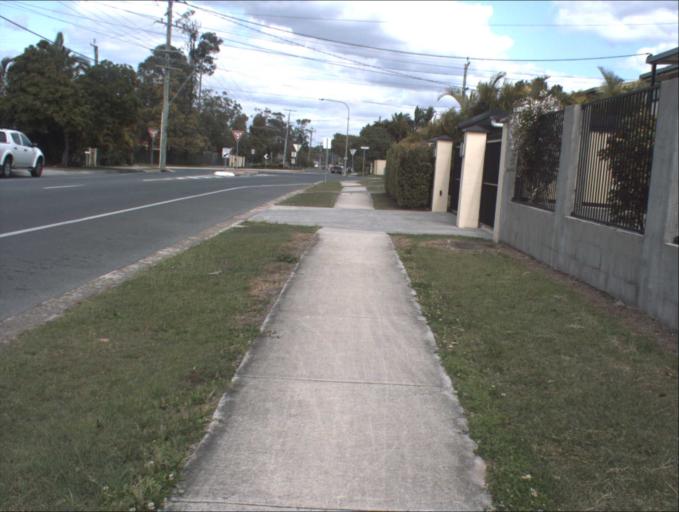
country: AU
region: Queensland
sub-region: Logan
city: Logan City
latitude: -27.6729
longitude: 153.0858
